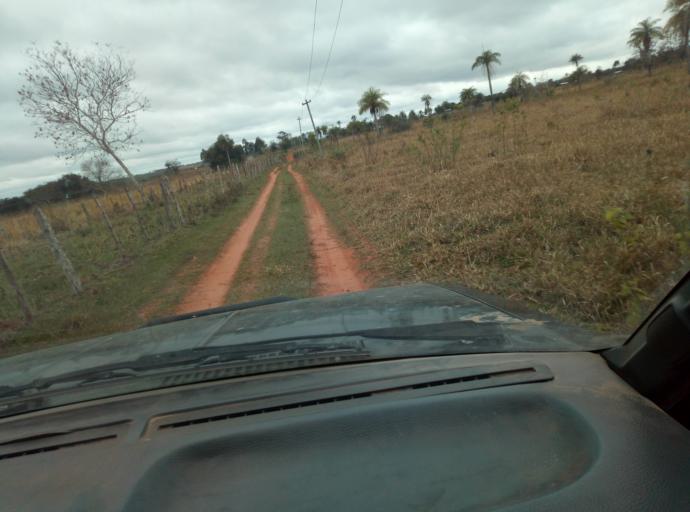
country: PY
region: Caaguazu
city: Doctor Cecilio Baez
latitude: -25.1448
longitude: -56.2955
